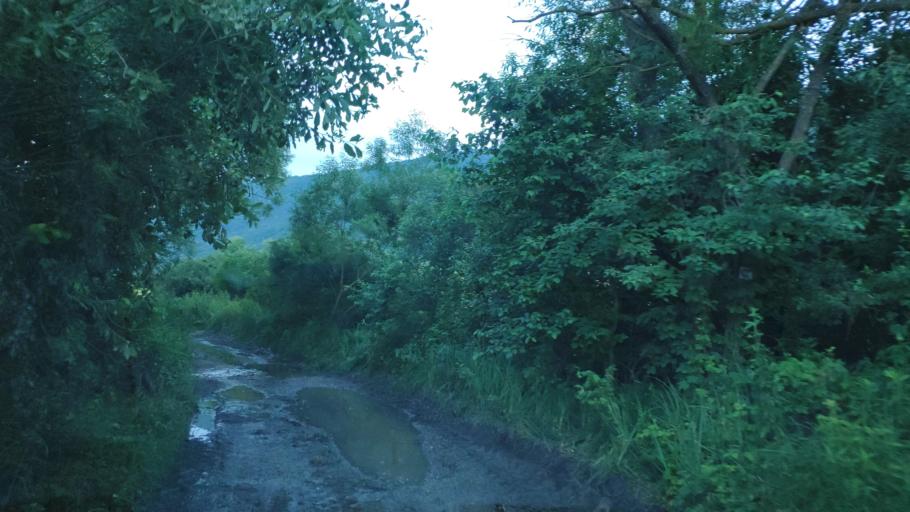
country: HU
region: Borsod-Abauj-Zemplen
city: Szendro
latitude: 48.5860
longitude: 20.7309
